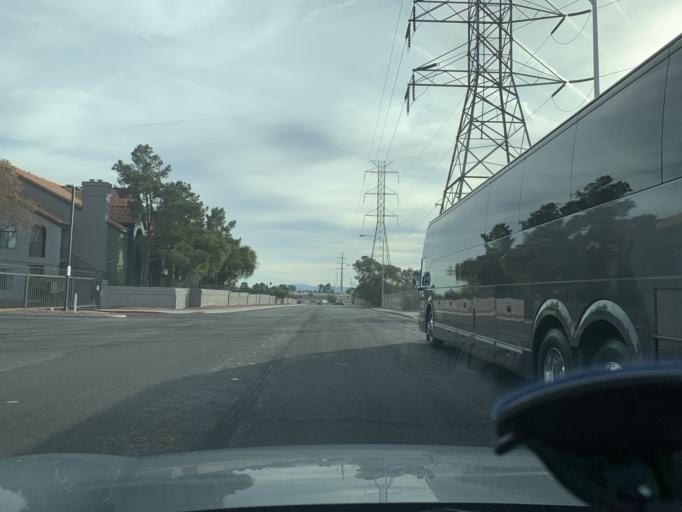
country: US
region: Nevada
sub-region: Clark County
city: Spring Valley
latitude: 36.1135
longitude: -115.2123
